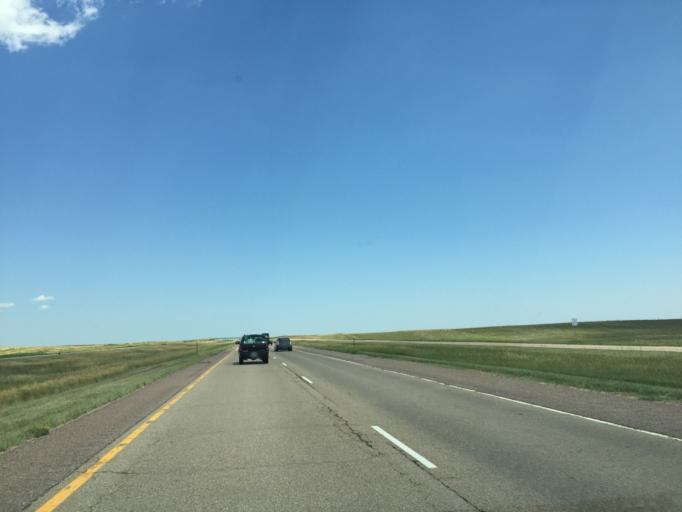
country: US
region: Colorado
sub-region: Lincoln County
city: Hugo
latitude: 39.2801
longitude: -103.3662
